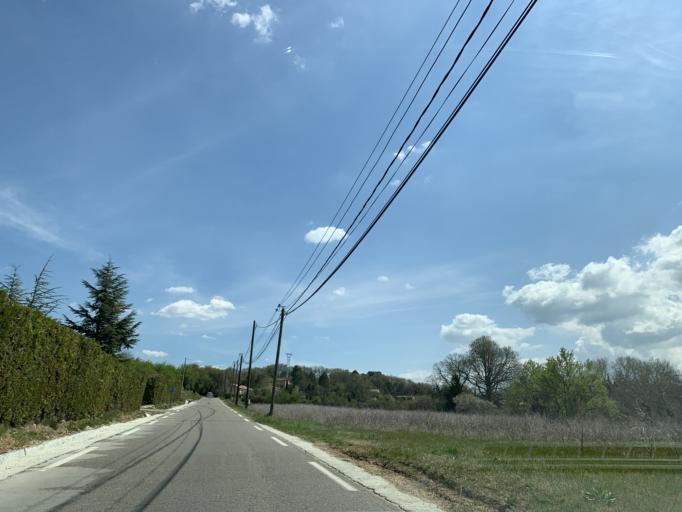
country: FR
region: Provence-Alpes-Cote d'Azur
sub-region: Departement du Vaucluse
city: Goult
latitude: 43.8681
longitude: 5.2465
